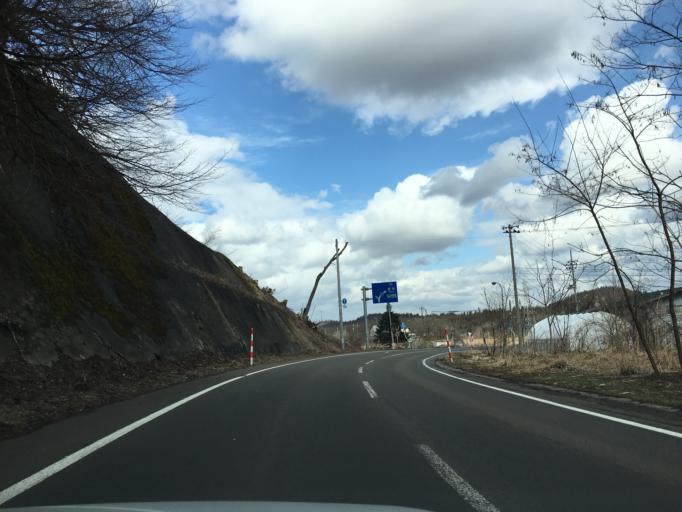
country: JP
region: Akita
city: Odate
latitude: 40.1981
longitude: 140.5348
